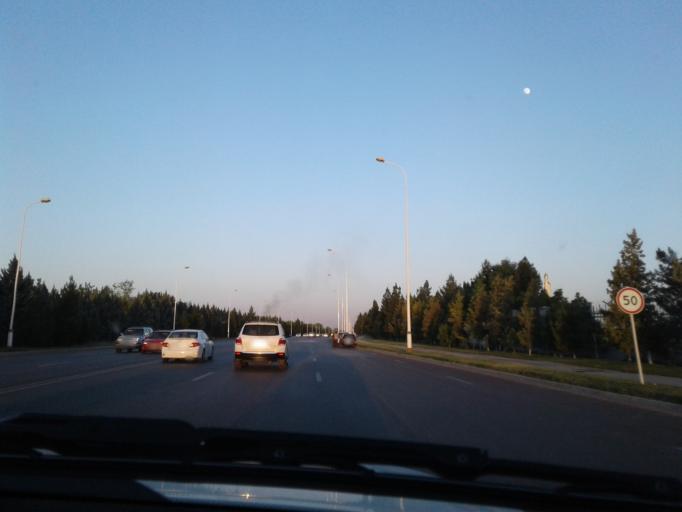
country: TM
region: Ahal
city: Abadan
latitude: 38.0241
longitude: 58.2448
